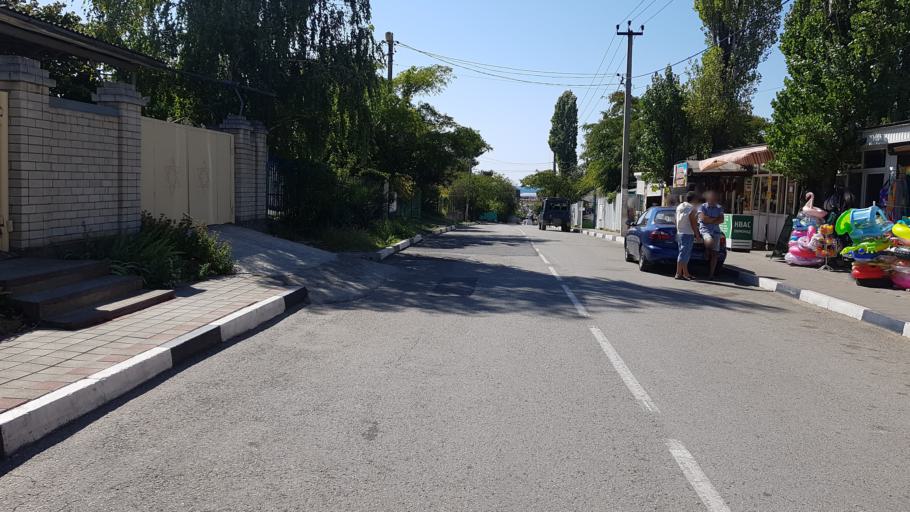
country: RU
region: Krasnodarskiy
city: Arkhipo-Osipovka
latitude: 44.3657
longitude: 38.5322
